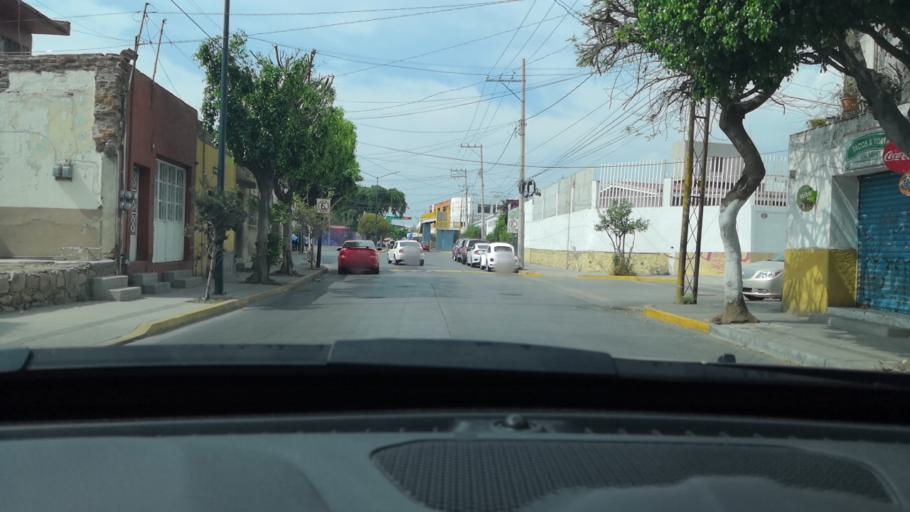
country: MX
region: Guanajuato
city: Leon
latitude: 21.1143
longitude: -101.6773
